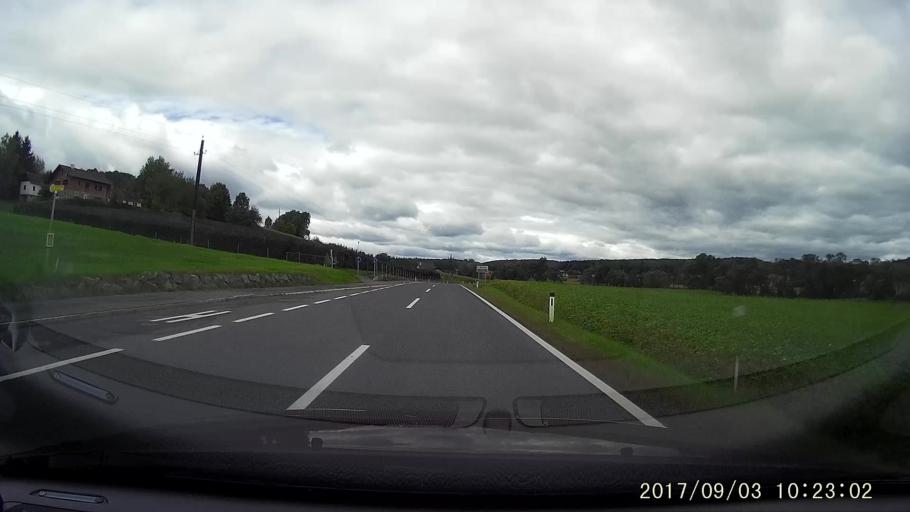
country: AT
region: Styria
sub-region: Politischer Bezirk Suedoststeiermark
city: Breitenfeld an der Rittschein
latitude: 47.0481
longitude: 15.9296
